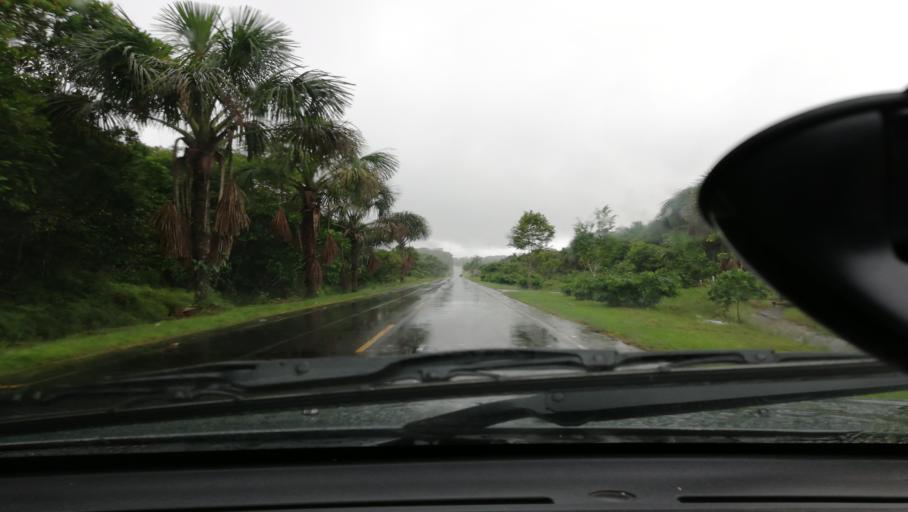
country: PE
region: Loreto
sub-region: Provincia de Maynas
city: San Juan
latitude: -3.9472
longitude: -73.4012
